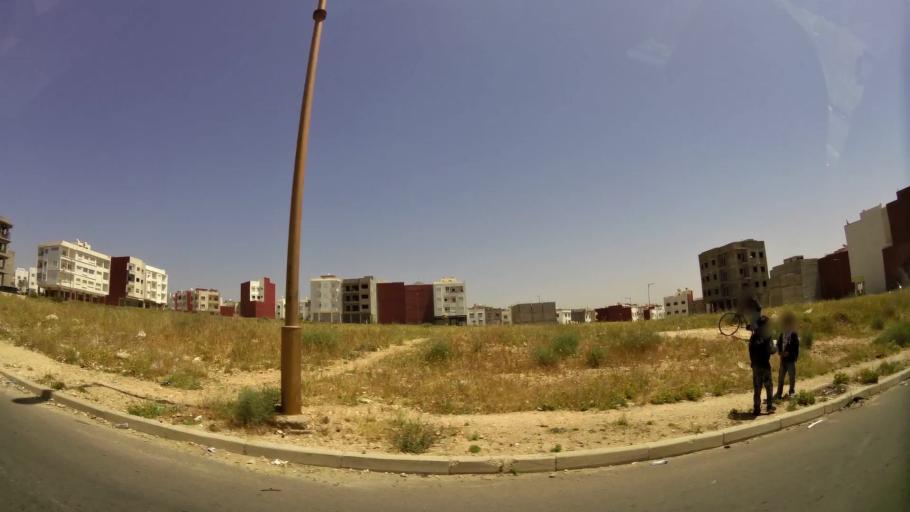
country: MA
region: Oued ed Dahab-Lagouira
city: Dakhla
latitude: 30.4391
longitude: -9.5564
